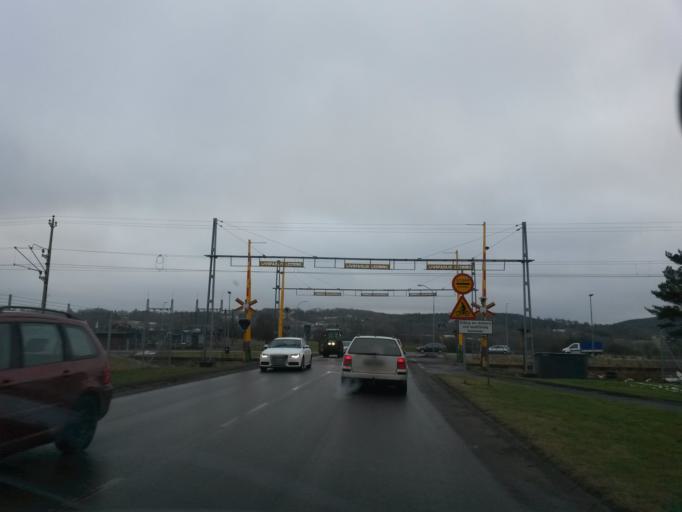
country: SE
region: Vaestra Goetaland
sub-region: Marks Kommun
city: Kinna
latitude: 57.4930
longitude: 12.6629
